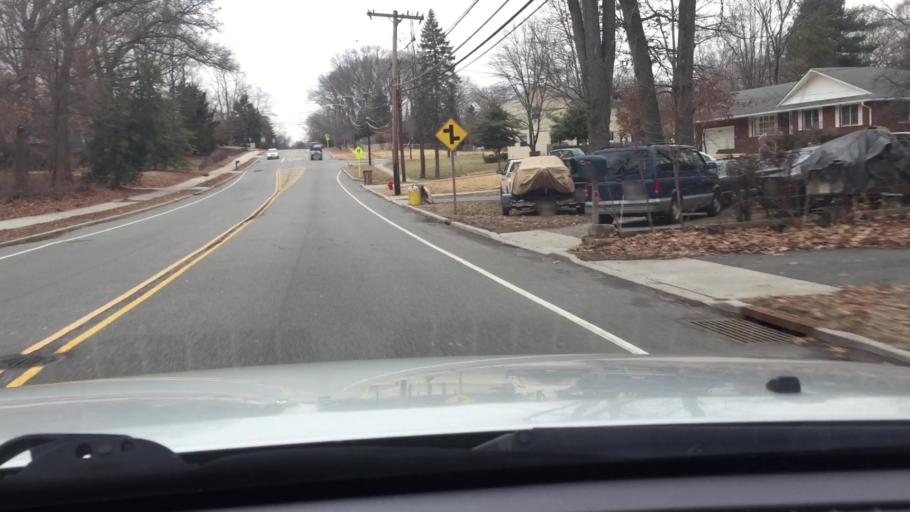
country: US
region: New Jersey
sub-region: Middlesex County
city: Spotswood
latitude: 40.4111
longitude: -74.3877
